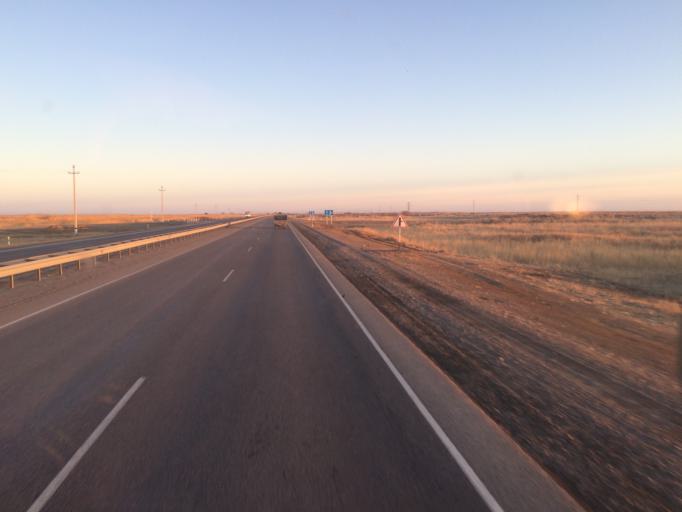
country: KZ
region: Qyzylorda
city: Shieli
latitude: 44.1706
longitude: 66.9071
